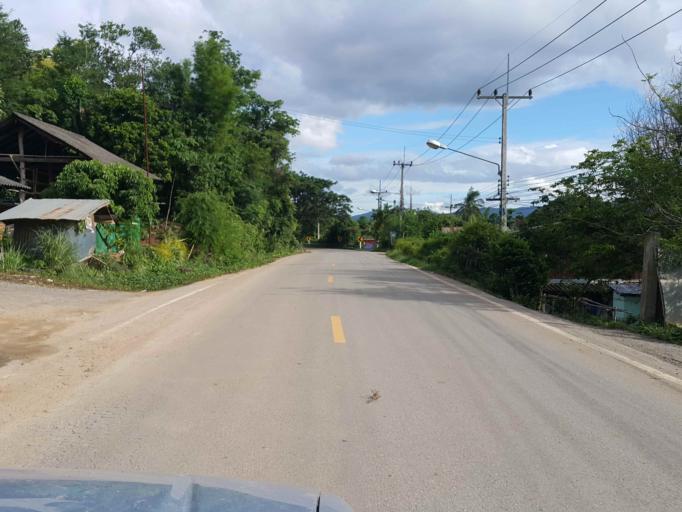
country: TH
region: Chiang Mai
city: Mae Chaem
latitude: 18.4817
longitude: 98.3764
